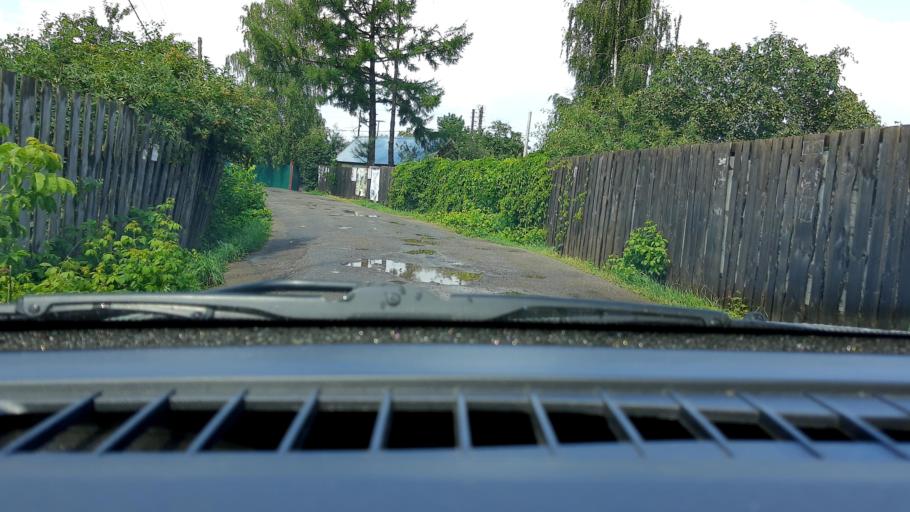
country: RU
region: Nizjnij Novgorod
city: Gorbatovka
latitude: 56.3817
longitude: 43.8273
